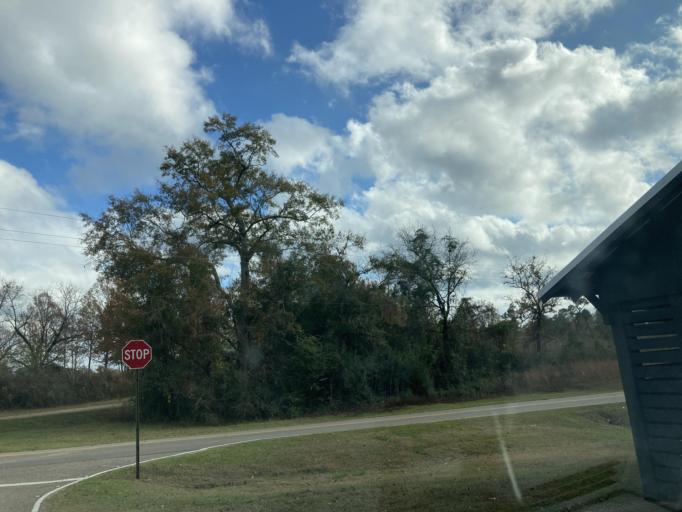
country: US
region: Mississippi
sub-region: Lamar County
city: Purvis
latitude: 31.1810
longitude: -89.5651
